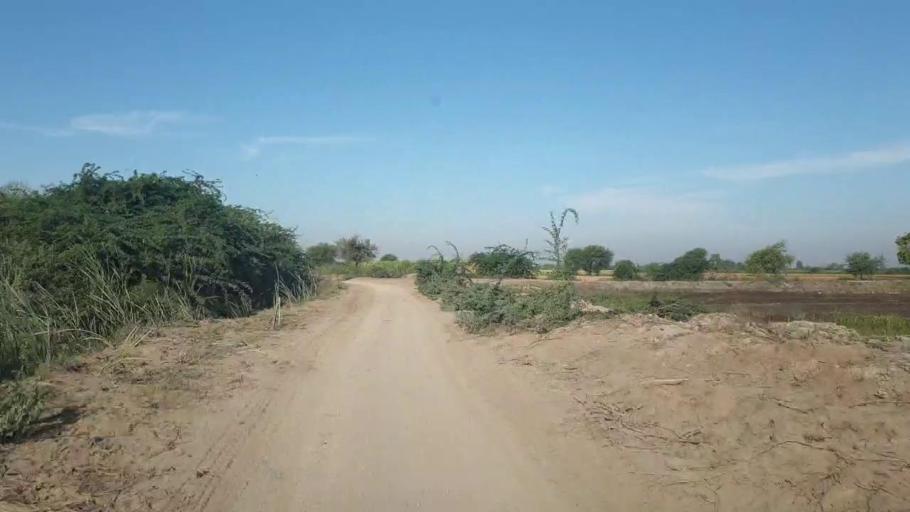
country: PK
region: Sindh
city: Talhar
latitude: 24.8234
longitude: 68.8291
